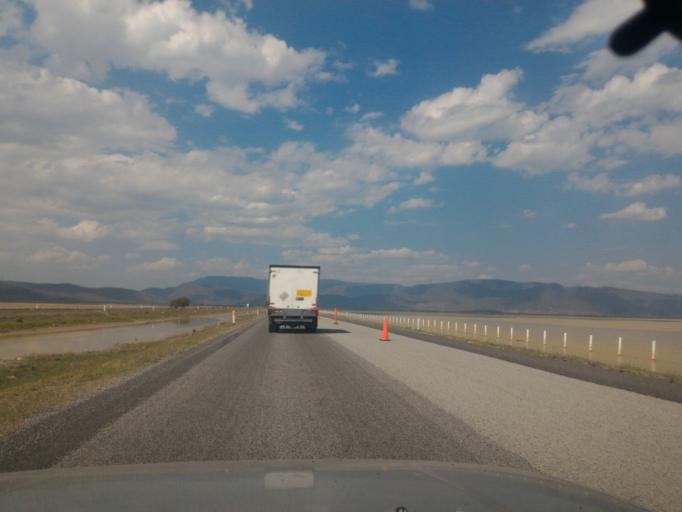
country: MX
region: Jalisco
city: Atoyac
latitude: 20.0970
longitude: -103.5144
